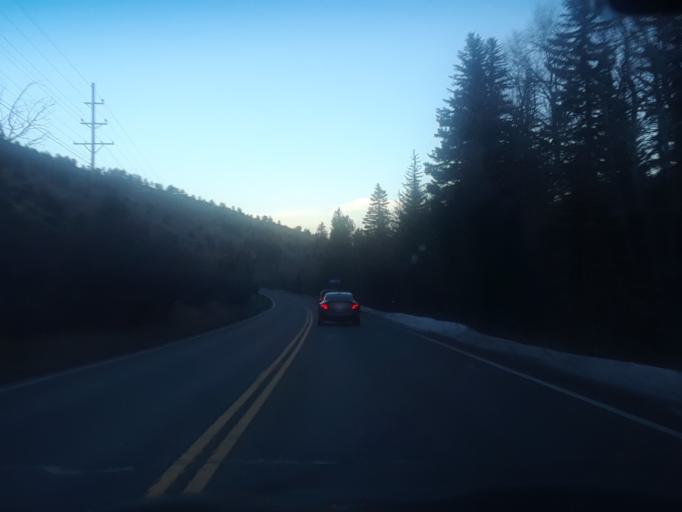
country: US
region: Colorado
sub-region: Clear Creek County
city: Georgetown
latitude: 39.4561
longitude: -105.6509
